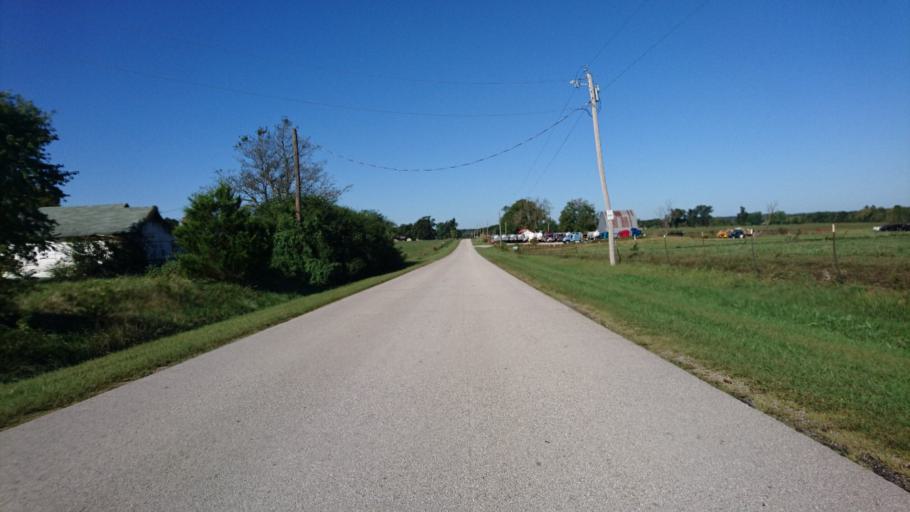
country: US
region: Missouri
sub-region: Greene County
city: Ash Grove
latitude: 37.1941
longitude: -93.6720
